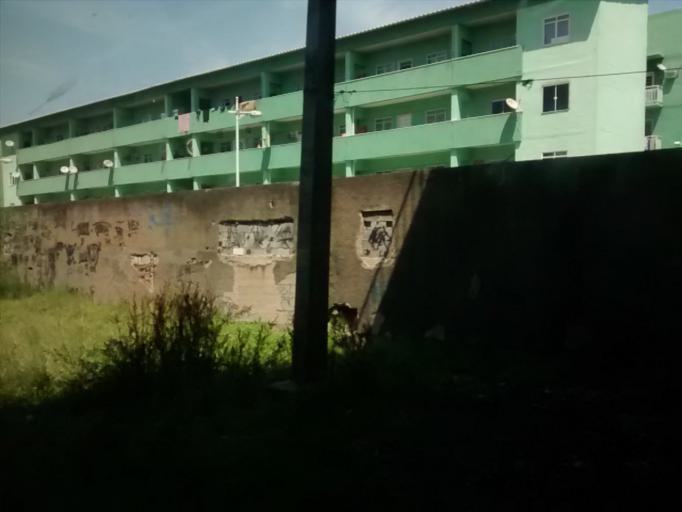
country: BR
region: Rio de Janeiro
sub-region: Rio De Janeiro
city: Rio de Janeiro
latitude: -22.8900
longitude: -43.2472
